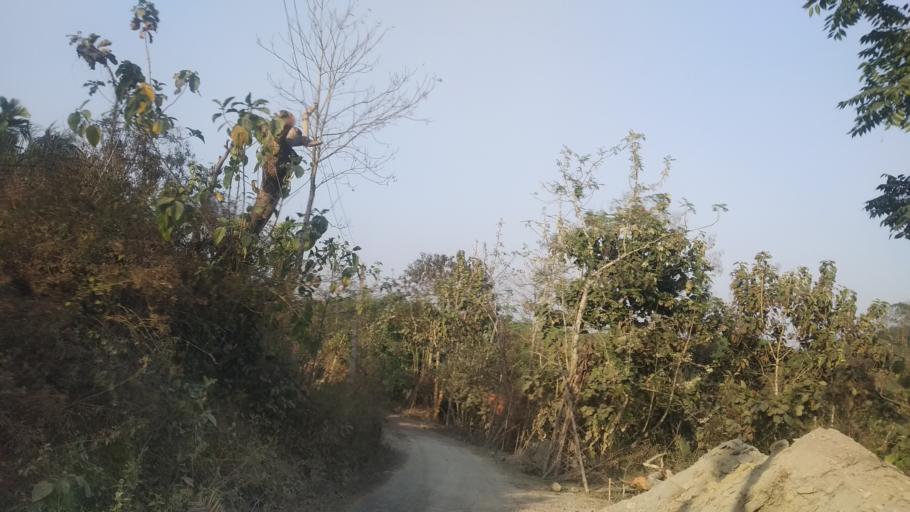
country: IN
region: Tripura
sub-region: West Tripura
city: Sonamura
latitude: 23.4394
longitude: 91.3616
